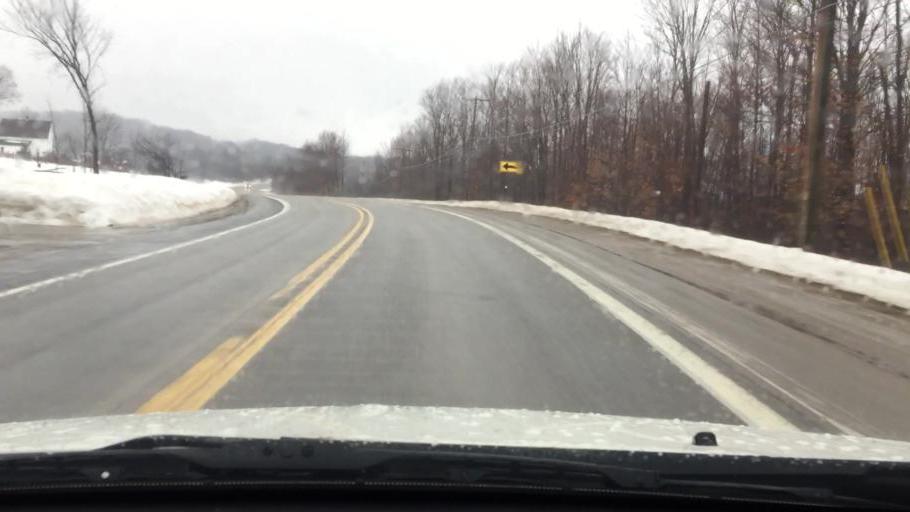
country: US
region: Michigan
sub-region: Charlevoix County
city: East Jordan
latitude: 45.1937
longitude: -85.1642
